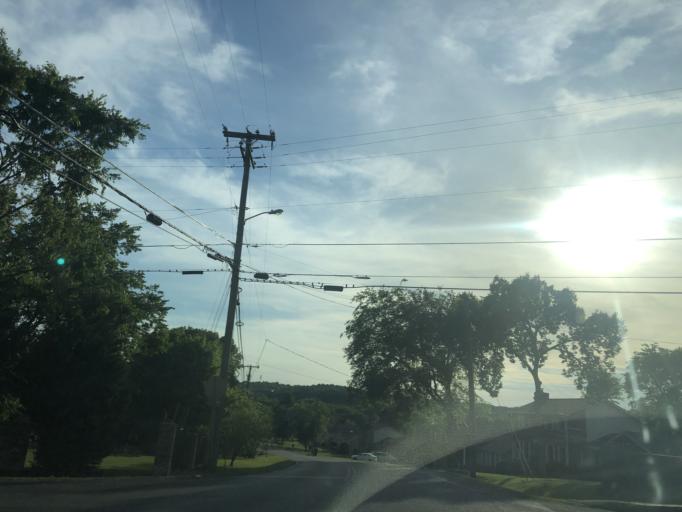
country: US
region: Tennessee
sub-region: Davidson County
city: Nashville
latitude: 36.2166
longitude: -86.8607
